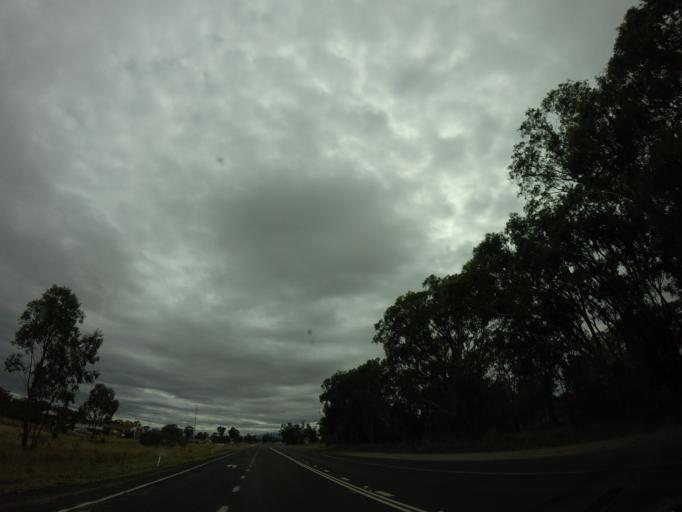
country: AU
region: New South Wales
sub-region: Narrabri
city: Narrabri
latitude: -30.3501
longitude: 149.7557
